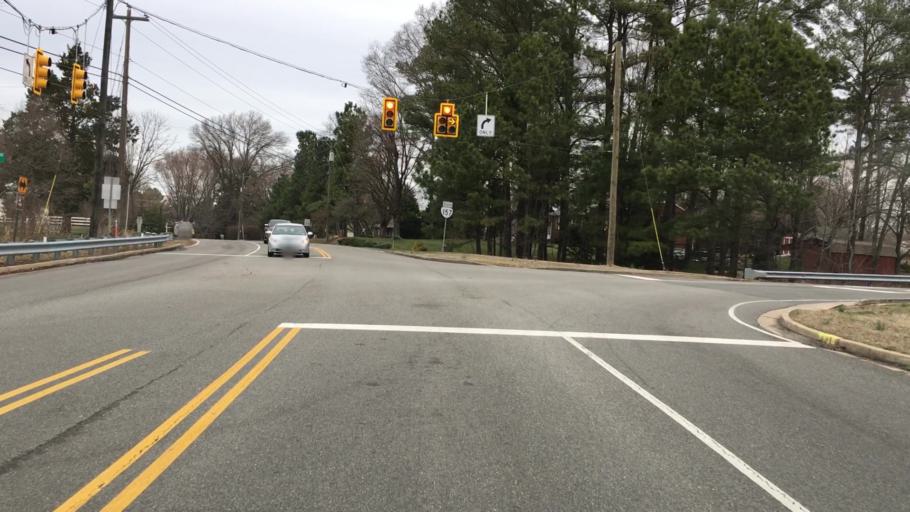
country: US
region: Virginia
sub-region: Henrico County
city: Glen Allen
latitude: 37.6712
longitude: -77.5417
